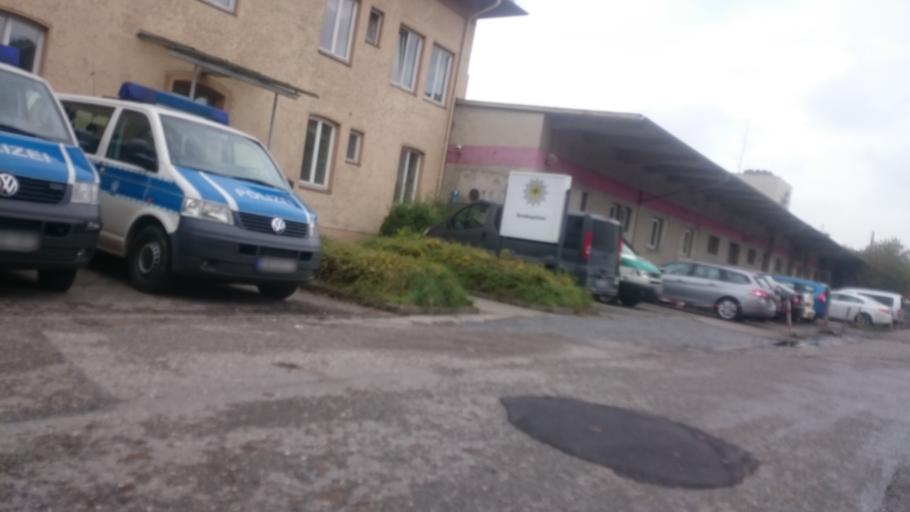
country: DE
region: Bavaria
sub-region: Swabia
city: Augsburg
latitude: 48.3638
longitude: 10.8885
